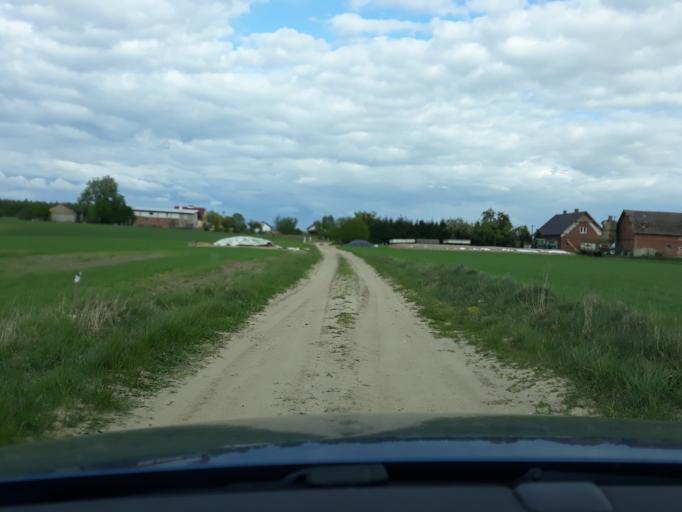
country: PL
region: Pomeranian Voivodeship
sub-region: Powiat czluchowski
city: Czluchow
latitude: 53.7543
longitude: 17.3644
